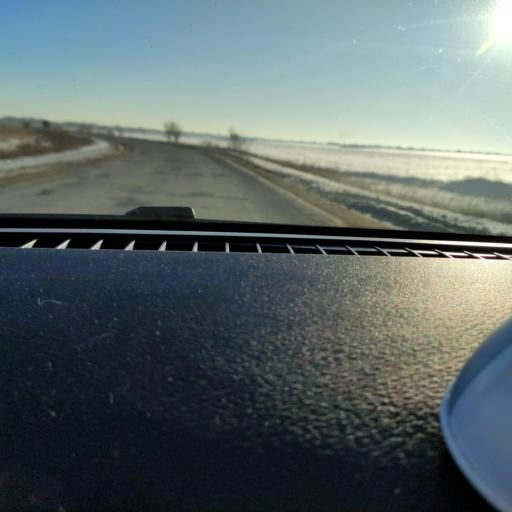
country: RU
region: Samara
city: Spiridonovka
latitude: 53.1268
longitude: 50.6185
